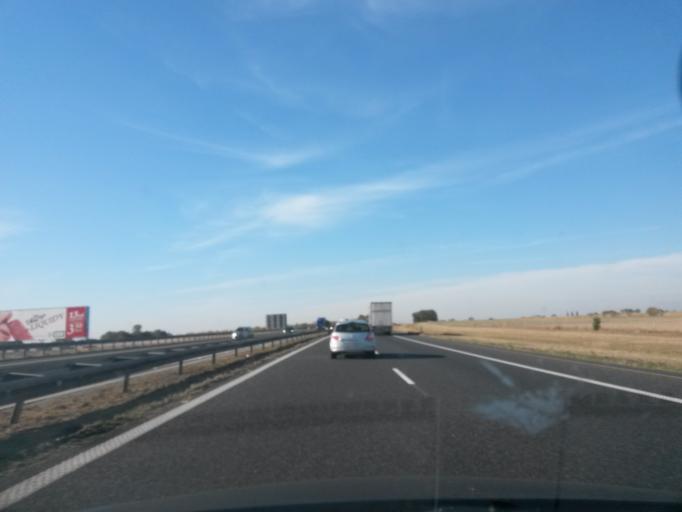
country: PL
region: Opole Voivodeship
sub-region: Powiat brzeski
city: Skarbimierz Osiedle
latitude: 50.7927
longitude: 17.3303
